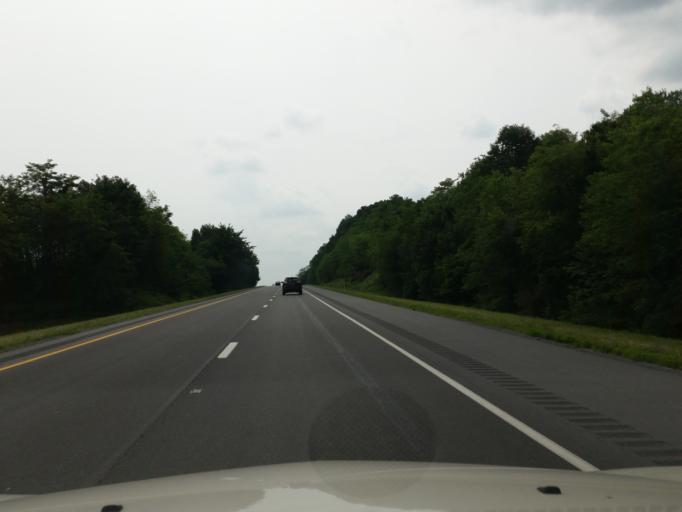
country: US
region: Pennsylvania
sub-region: Juniata County
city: Mifflintown
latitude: 40.5584
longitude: -77.2828
